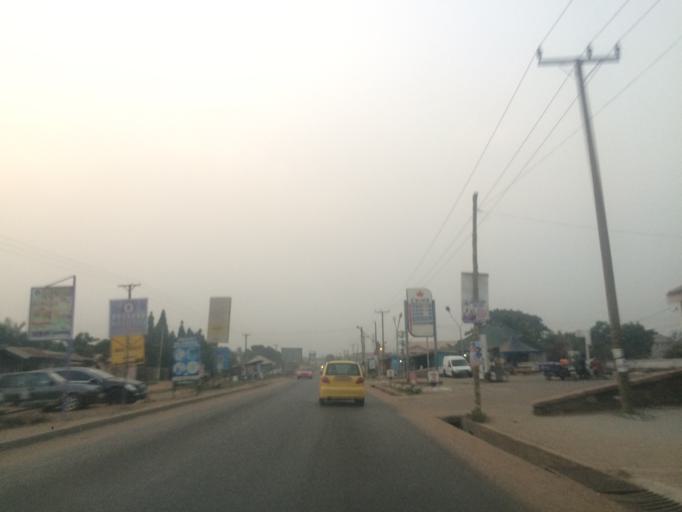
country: GH
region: Greater Accra
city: Teshi Old Town
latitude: 5.5932
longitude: -0.1005
